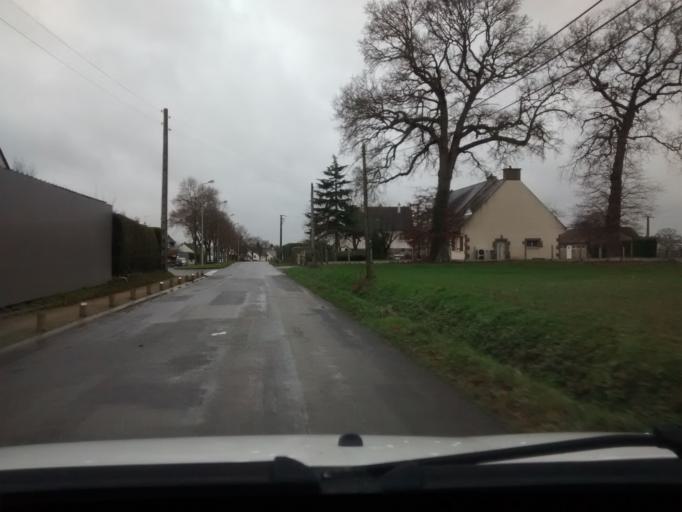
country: FR
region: Brittany
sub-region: Departement d'Ille-et-Vilaine
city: Servon-sur-Vilaine
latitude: 48.1246
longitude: -1.4489
